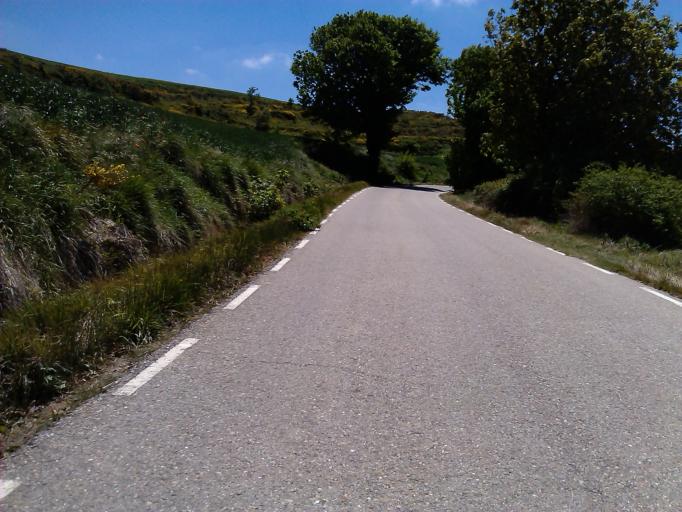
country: ES
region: Castille and Leon
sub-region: Provincia de Burgos
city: Cerraton de Juarros
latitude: 42.4267
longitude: -3.3631
